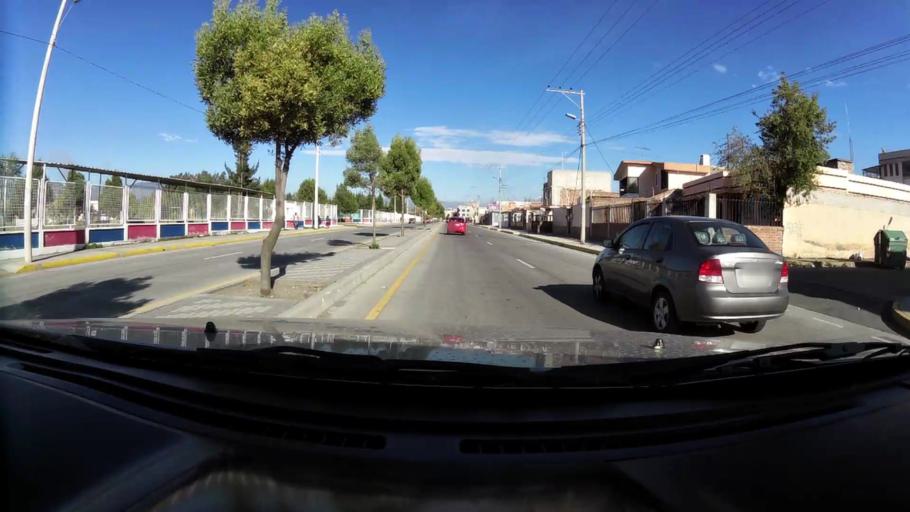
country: EC
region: Chimborazo
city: Riobamba
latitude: -1.6876
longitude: -78.6402
